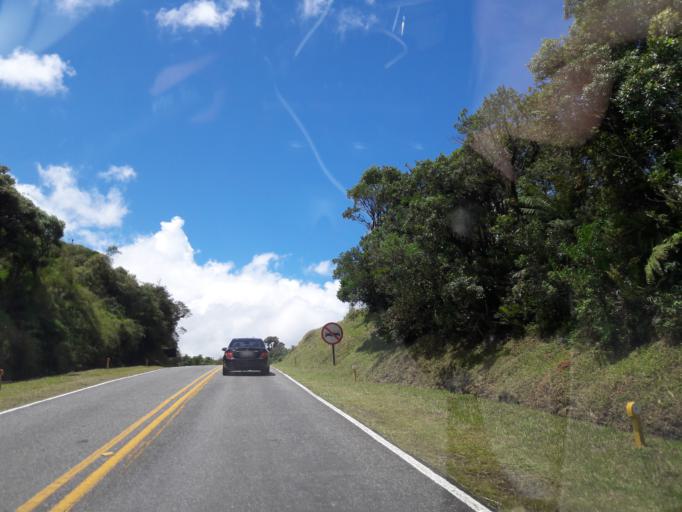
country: BR
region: Parana
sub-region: Campina Grande Do Sul
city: Campina Grande do Sul
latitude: -25.3331
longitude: -48.9066
